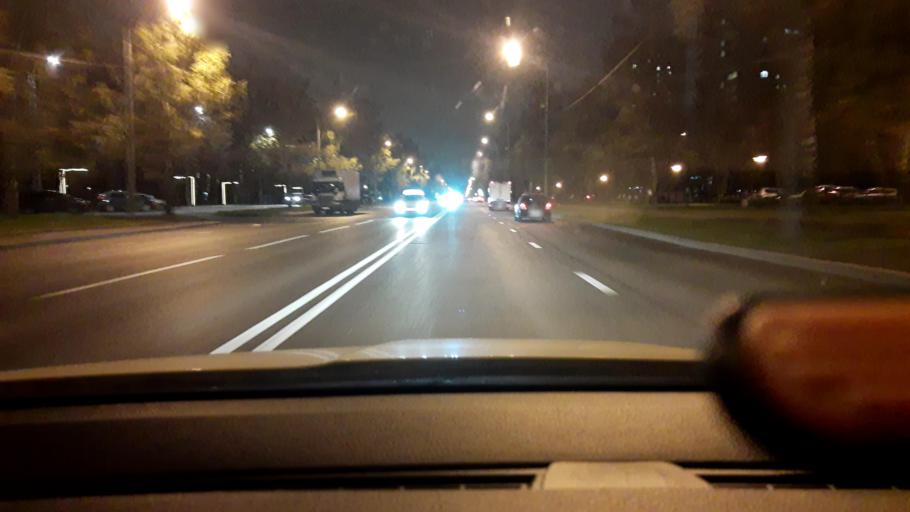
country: RU
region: Moskovskaya
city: Levoberezhnyy
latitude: 55.8620
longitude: 37.4481
